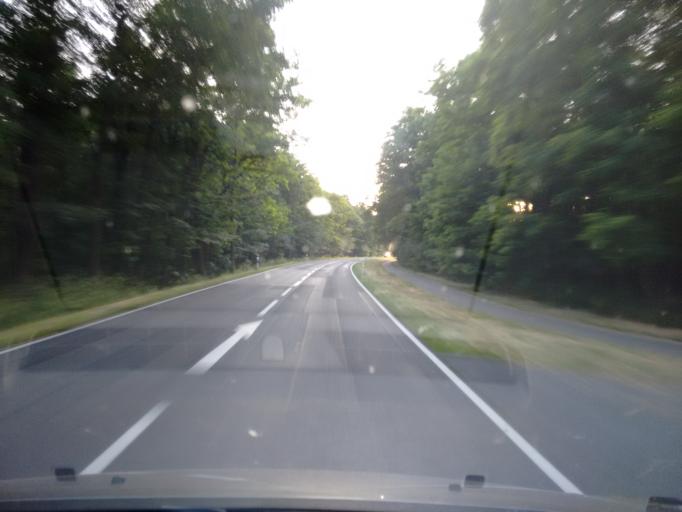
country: DE
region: Brandenburg
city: Mixdorf
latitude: 52.1354
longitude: 14.4371
